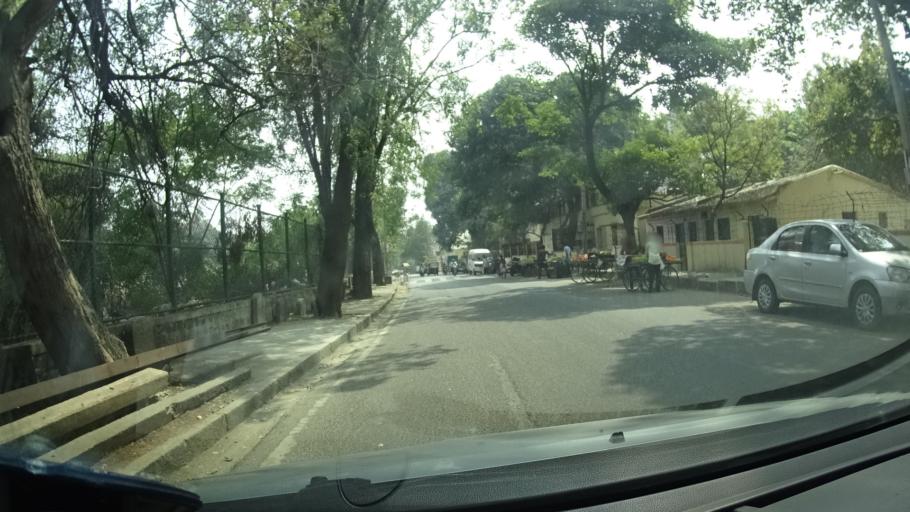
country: IN
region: Karnataka
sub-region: Bangalore Urban
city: Bangalore
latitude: 12.9987
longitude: 77.5644
